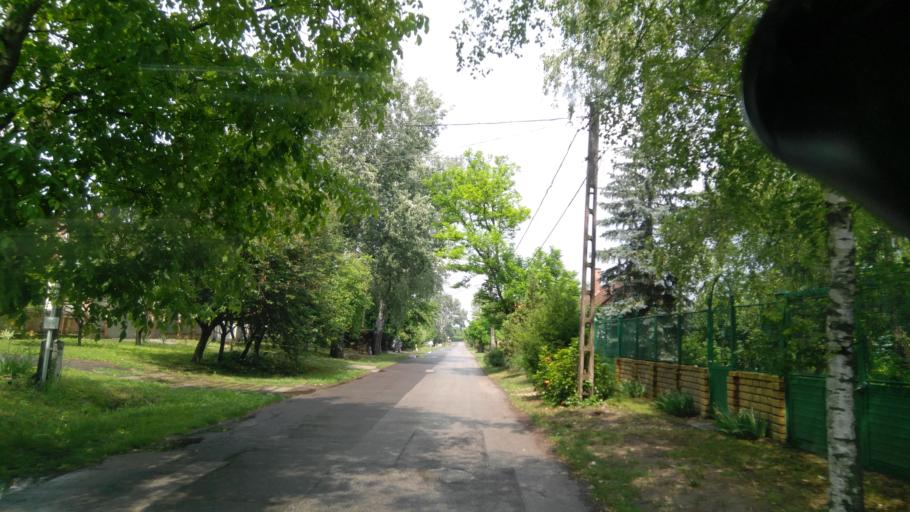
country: HU
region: Bekes
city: Bekescsaba
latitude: 46.6677
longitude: 21.1743
